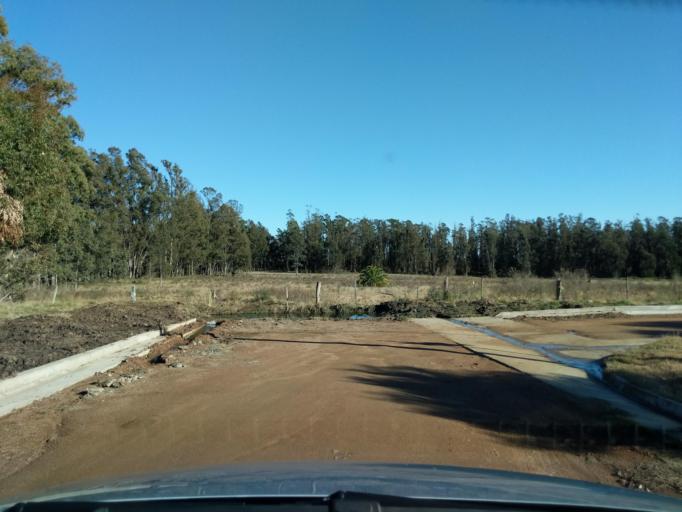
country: UY
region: Florida
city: Florida
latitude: -34.0875
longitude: -56.2406
